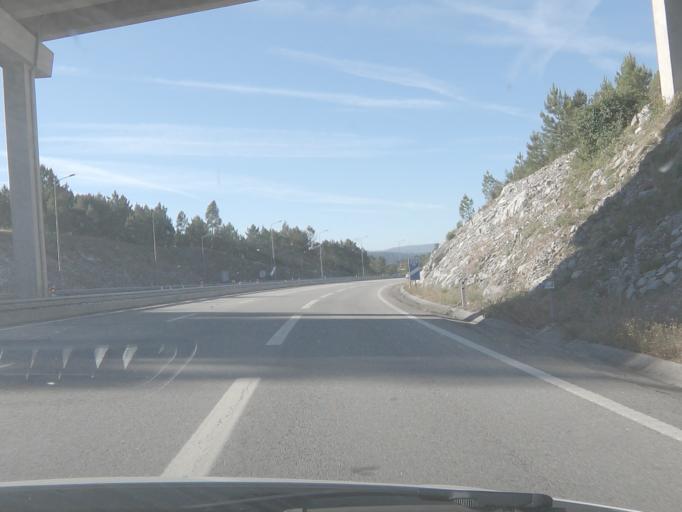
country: PT
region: Viseu
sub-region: Castro Daire
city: Castro Daire
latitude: 40.8177
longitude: -7.9398
